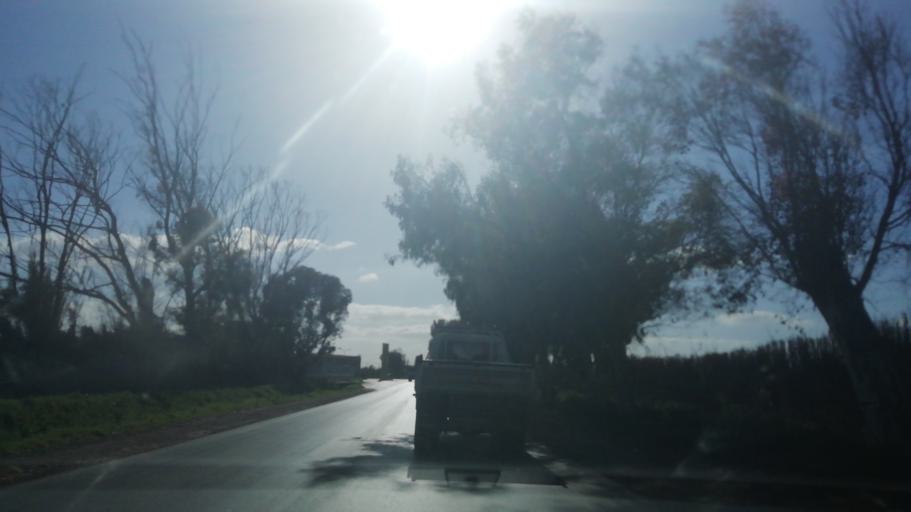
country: DZ
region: Mostaganem
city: Mostaganem
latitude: 35.9746
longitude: 0.2716
